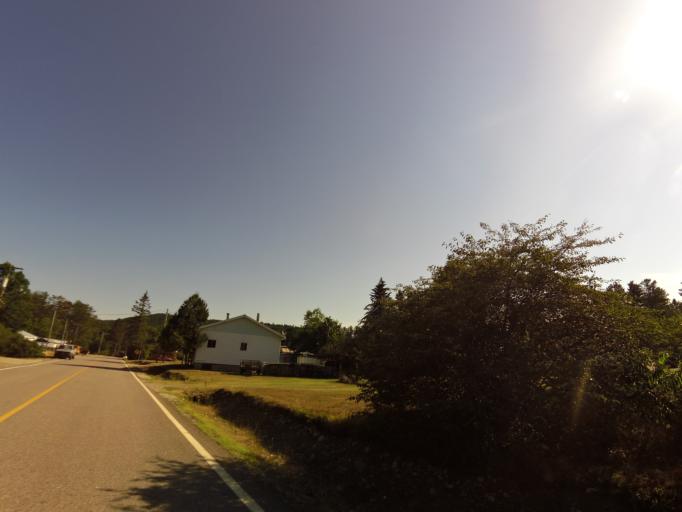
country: CA
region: Ontario
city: Deep River
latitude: 46.1940
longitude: -77.6922
